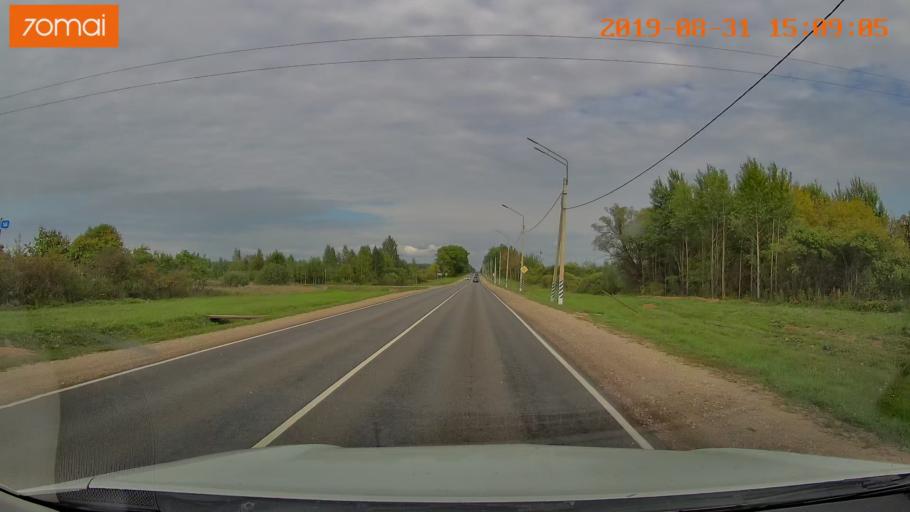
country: RU
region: Kaluga
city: Spas-Demensk
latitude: 54.3980
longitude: 34.1943
